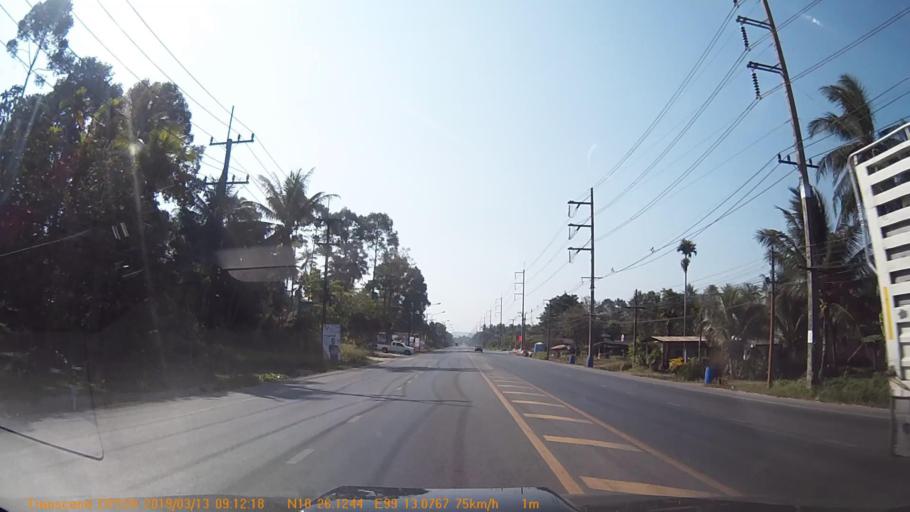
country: TH
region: Chumphon
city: Chumphon
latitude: 10.4352
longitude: 99.2181
